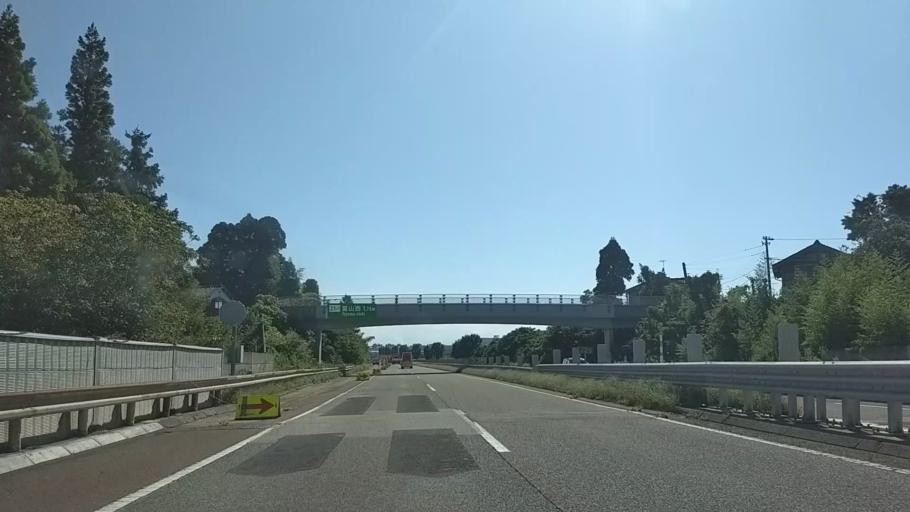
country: JP
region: Toyama
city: Kuragaki-kosugi
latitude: 36.6813
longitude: 137.1136
